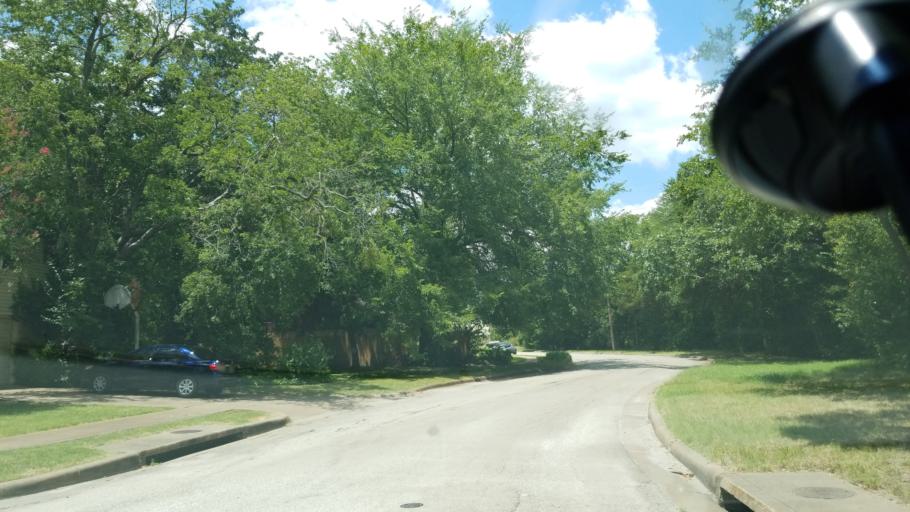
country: US
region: Texas
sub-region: Dallas County
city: Cockrell Hill
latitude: 32.6990
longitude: -96.8480
